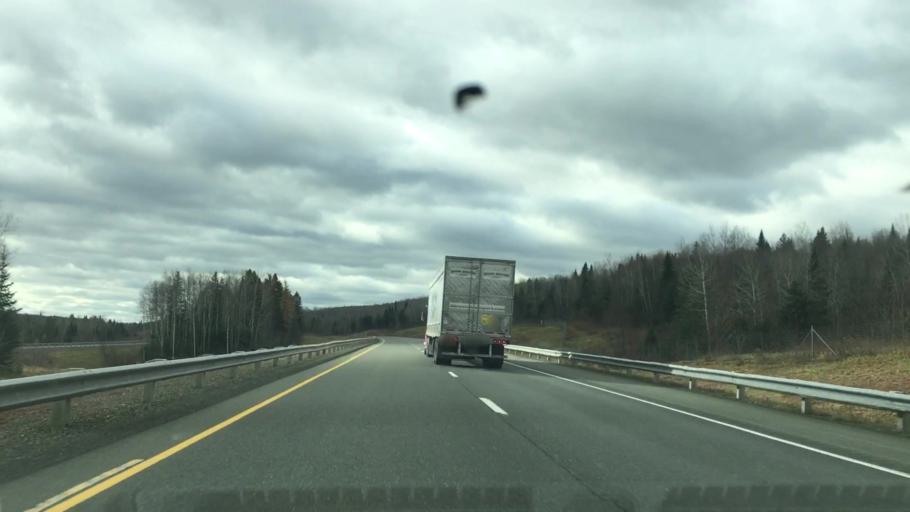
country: US
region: Maine
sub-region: Aroostook County
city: Fort Fairfield
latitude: 46.6537
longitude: -67.7385
